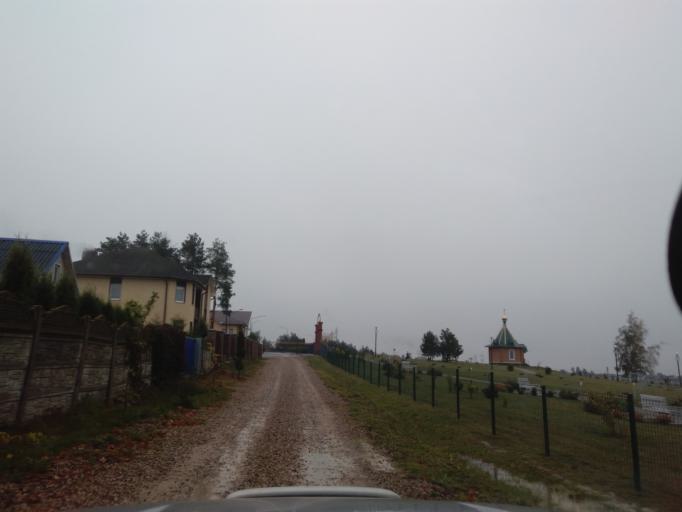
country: BY
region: Minsk
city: Kapyl'
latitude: 53.1556
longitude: 27.0955
